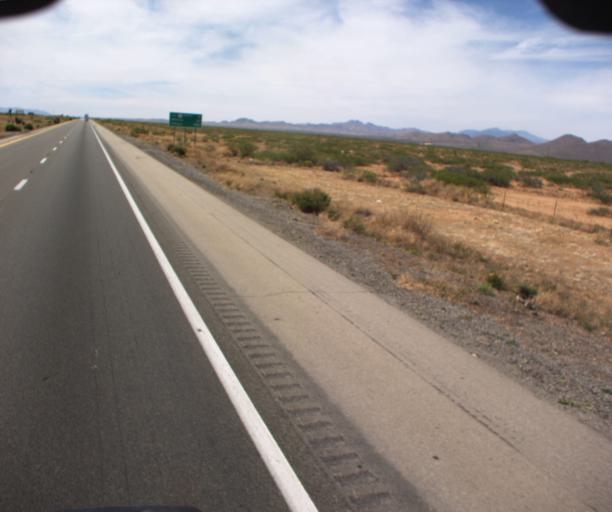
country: US
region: Arizona
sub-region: Cochise County
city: Willcox
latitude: 32.3361
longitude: -109.5380
